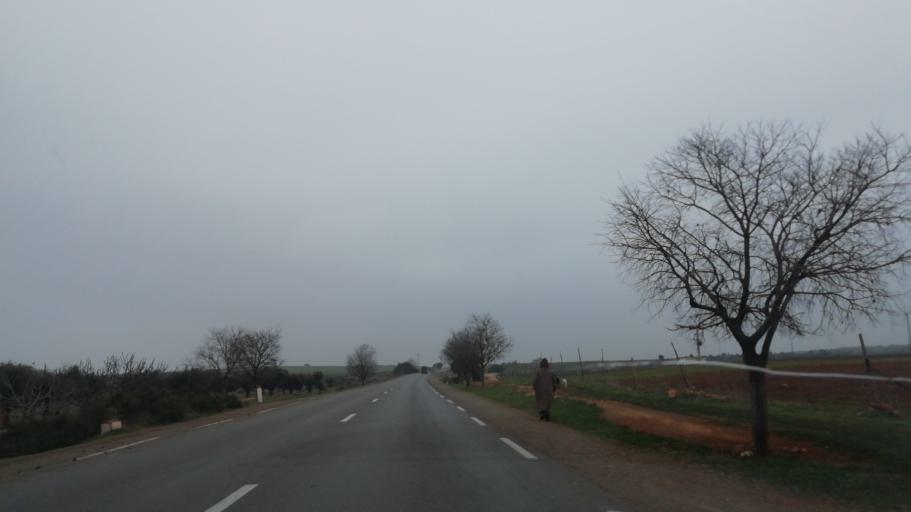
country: DZ
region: Mascara
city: Mascara
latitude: 35.3077
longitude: 0.4120
